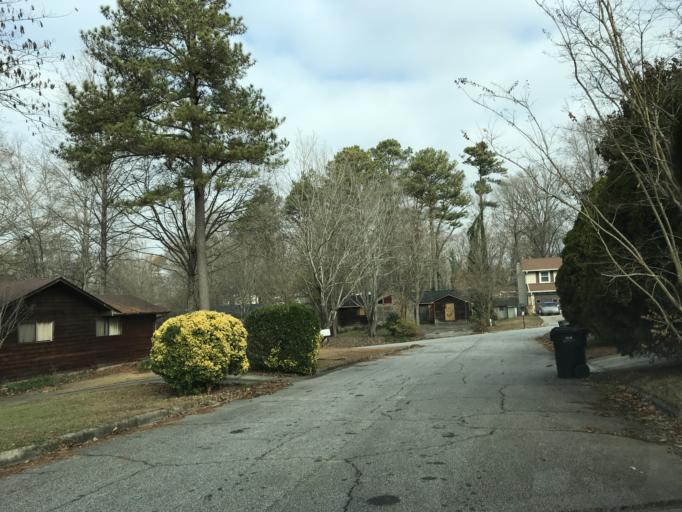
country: US
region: Georgia
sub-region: Clayton County
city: Jonesboro
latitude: 33.5571
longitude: -84.3742
